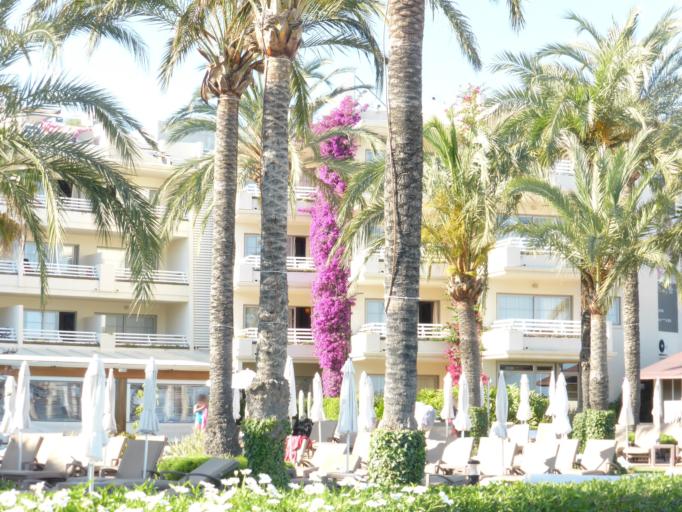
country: ES
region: Balearic Islands
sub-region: Illes Balears
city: Port d'Alcudia
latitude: 39.8404
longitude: 3.1275
